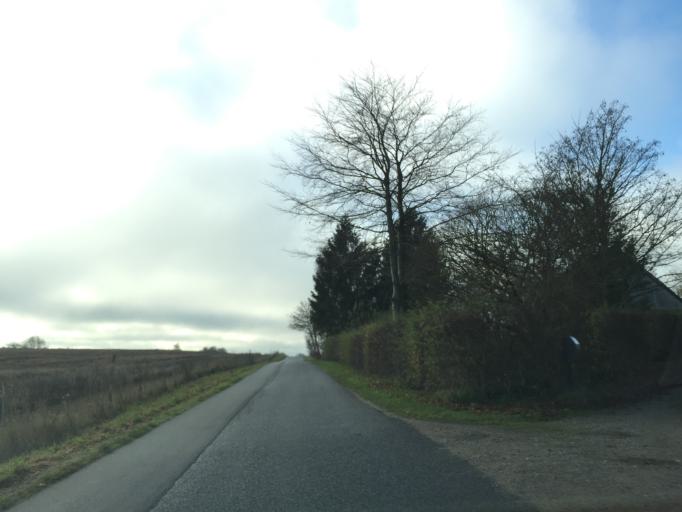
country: DK
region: Central Jutland
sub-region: Skanderborg Kommune
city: Ry
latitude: 56.1714
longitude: 9.7979
